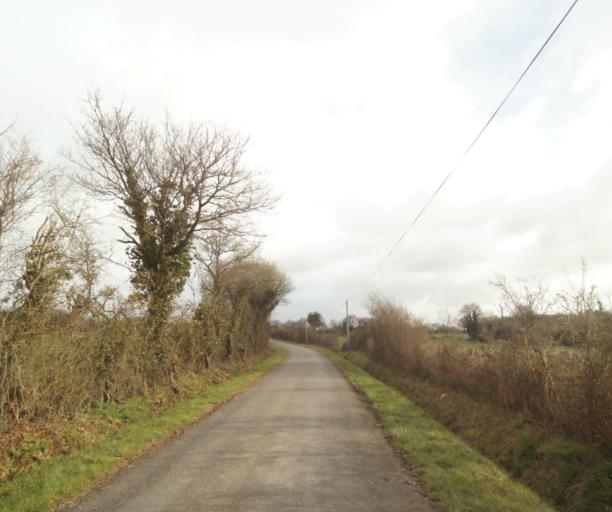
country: FR
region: Pays de la Loire
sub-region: Departement de la Loire-Atlantique
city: Bouvron
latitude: 47.4005
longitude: -1.8597
